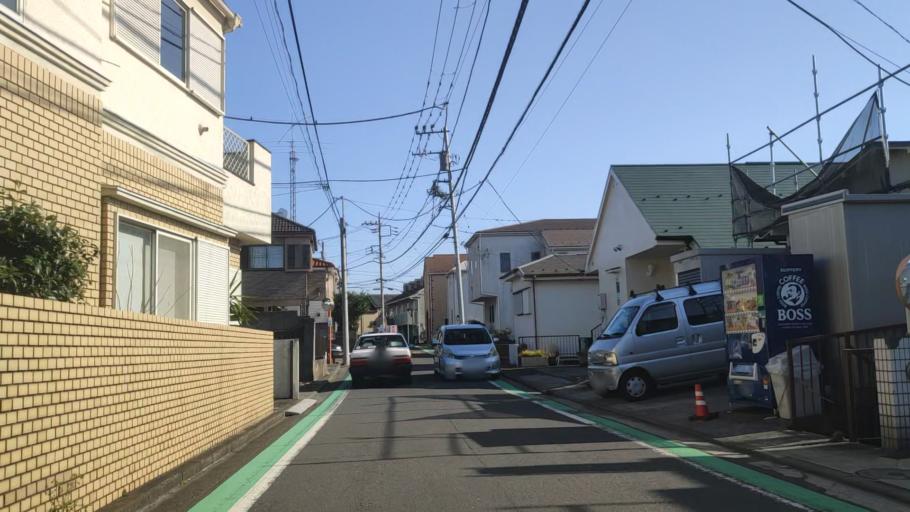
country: JP
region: Kanagawa
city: Yokohama
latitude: 35.4637
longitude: 139.5995
